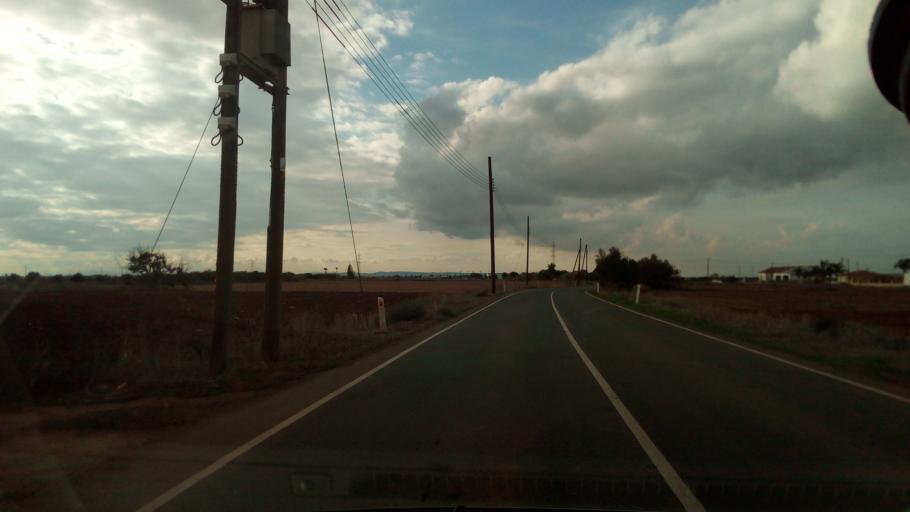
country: CY
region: Ammochostos
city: Liopetri
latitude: 35.0418
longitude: 33.8768
